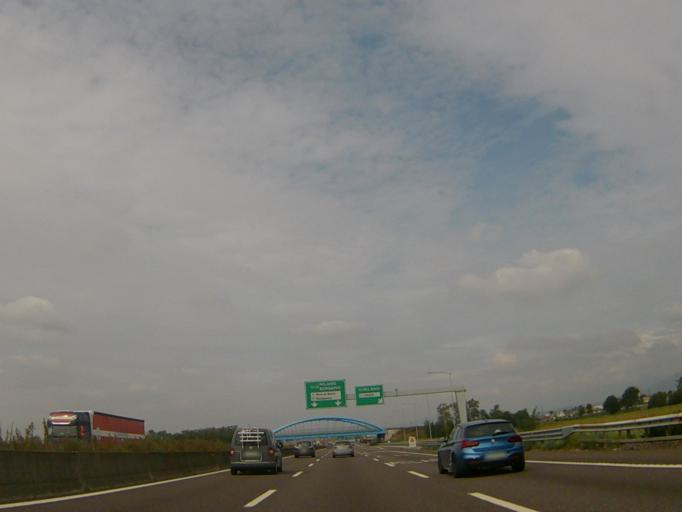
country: IT
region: Lombardy
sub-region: Provincia di Brescia
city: Castegnato
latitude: 45.5418
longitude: 10.1305
